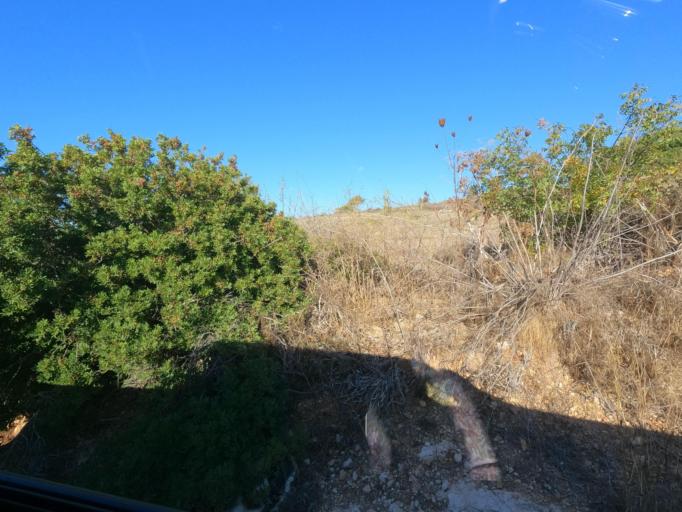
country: CY
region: Pafos
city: Mesogi
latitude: 34.7995
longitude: 32.4926
